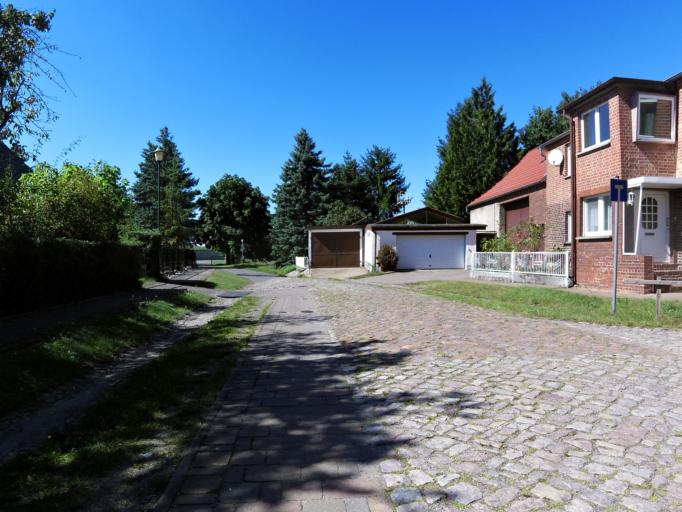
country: DE
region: Saxony-Anhalt
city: Muhlanger
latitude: 51.8390
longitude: 12.7555
